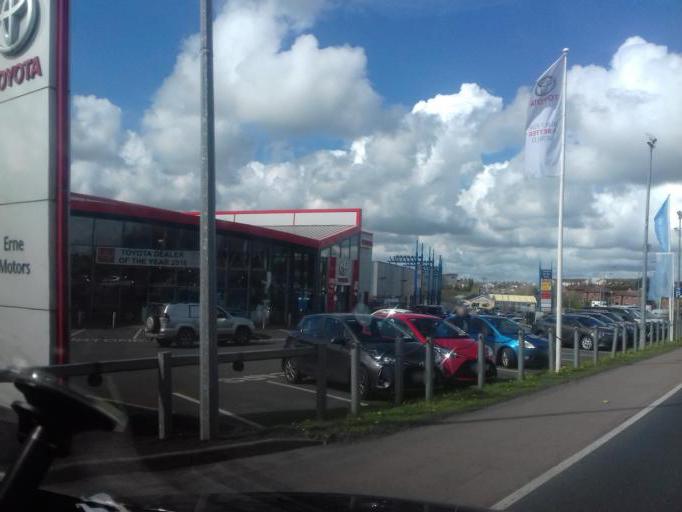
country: IE
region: Ulster
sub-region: An Cabhan
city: Cavan
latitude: 53.9842
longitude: -7.3477
